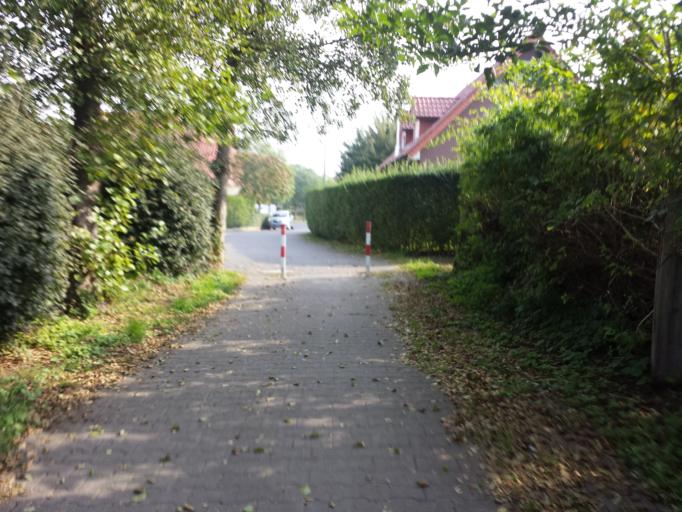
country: DE
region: North Rhine-Westphalia
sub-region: Regierungsbezirk Detmold
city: Guetersloh
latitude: 51.9098
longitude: 8.3547
